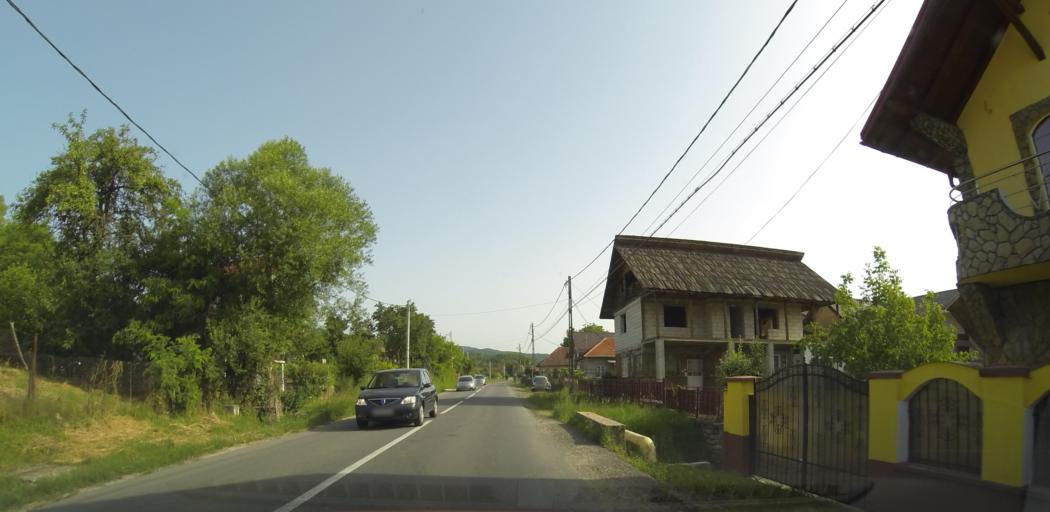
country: RO
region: Valcea
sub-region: Comuna Pausesti-Maglasi
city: Pausesti-Maglasi
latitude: 45.1477
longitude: 24.2457
